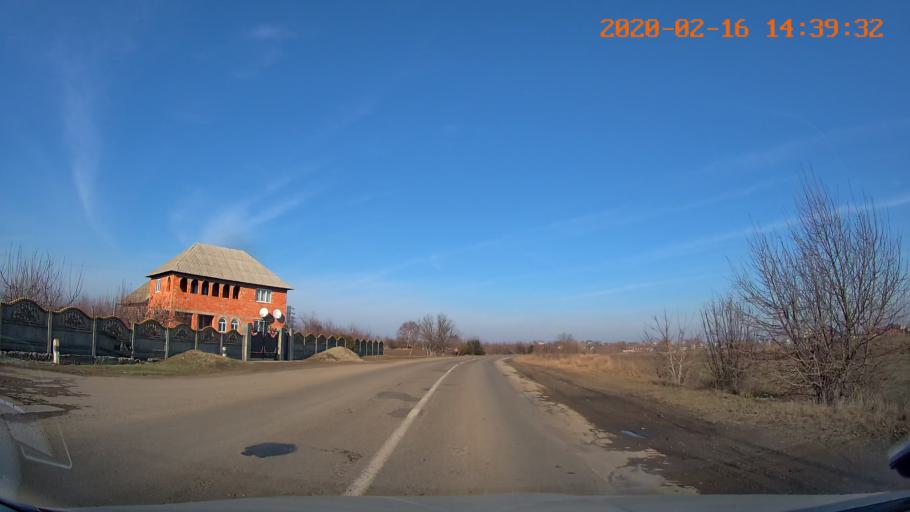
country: RO
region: Botosani
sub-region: Comuna Darabani
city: Bajura
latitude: 48.2442
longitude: 26.5499
